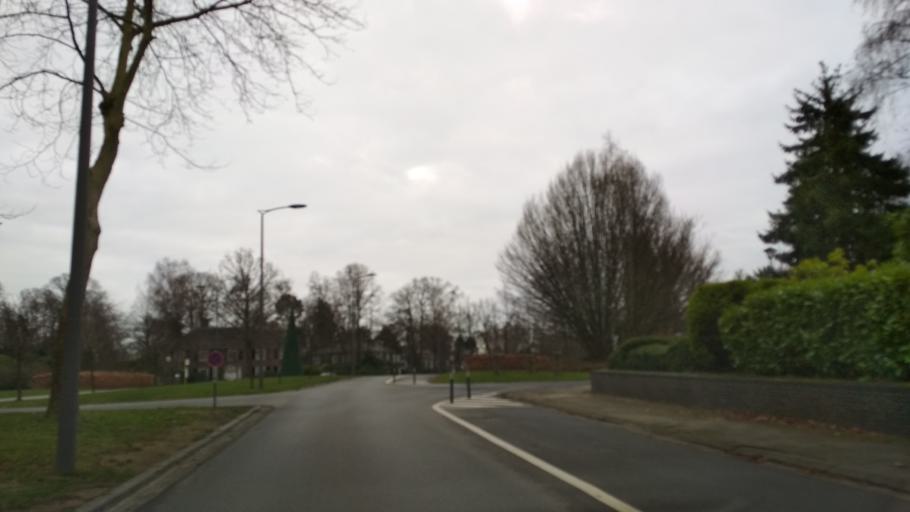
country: BE
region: Flanders
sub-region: Provincie Vlaams-Brabant
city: Wezembeek-Oppem
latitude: 50.8315
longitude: 4.4711
